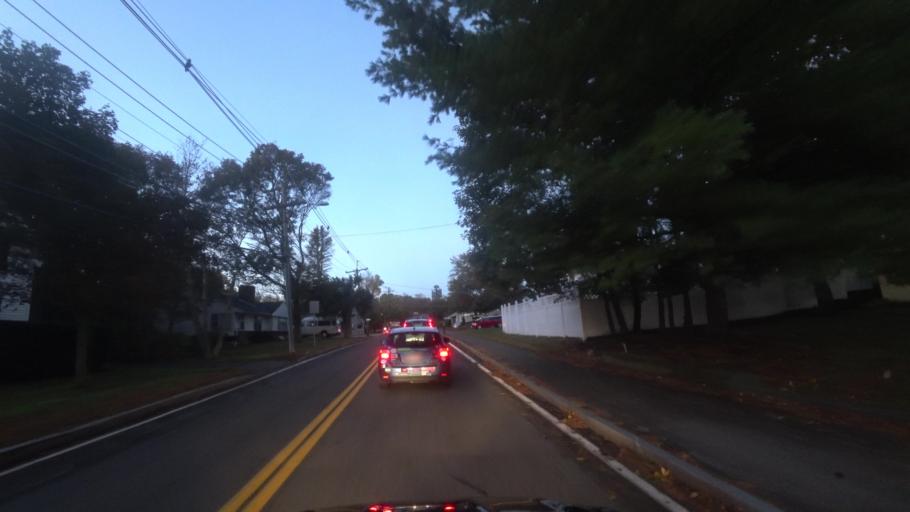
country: US
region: Massachusetts
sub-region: Middlesex County
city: Wakefield
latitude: 42.5013
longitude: -71.0480
